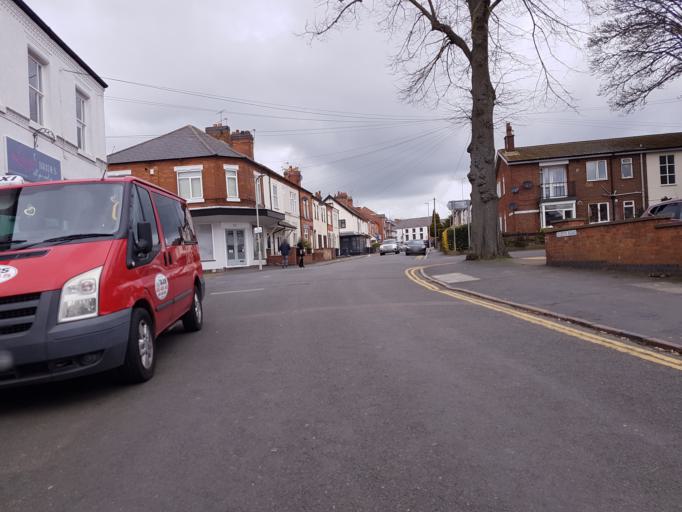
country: GB
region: England
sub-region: Leicestershire
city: Hinckley
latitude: 52.5406
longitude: -1.3654
